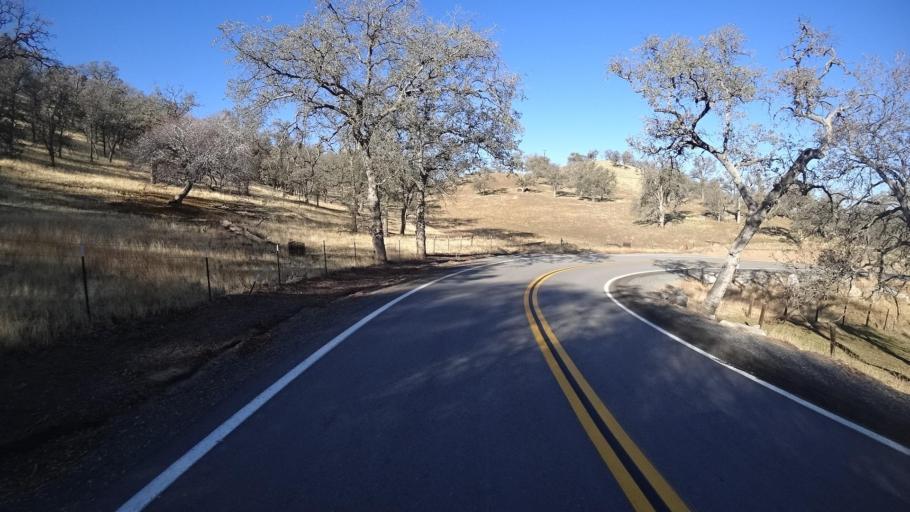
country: US
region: California
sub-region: Kern County
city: Alta Sierra
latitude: 35.7155
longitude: -118.7911
